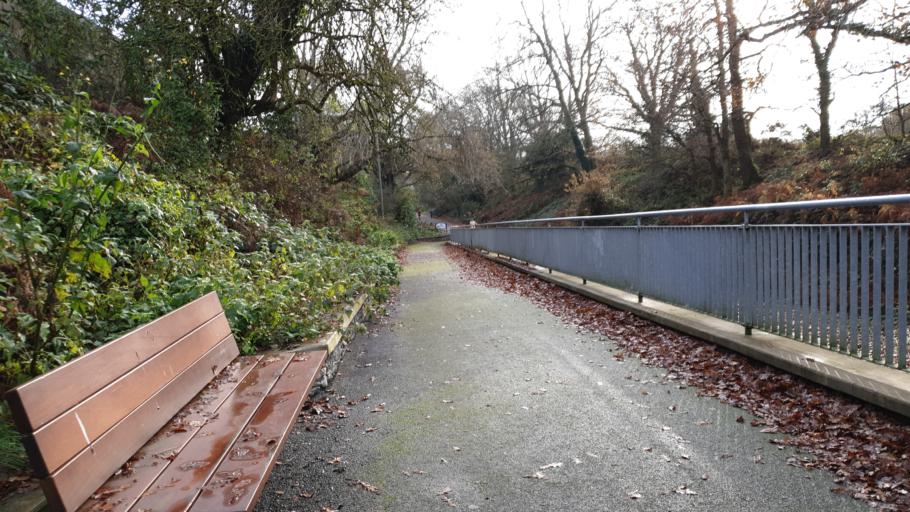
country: IE
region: Munster
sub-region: County Cork
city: Passage West
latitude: 51.8853
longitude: -8.4062
